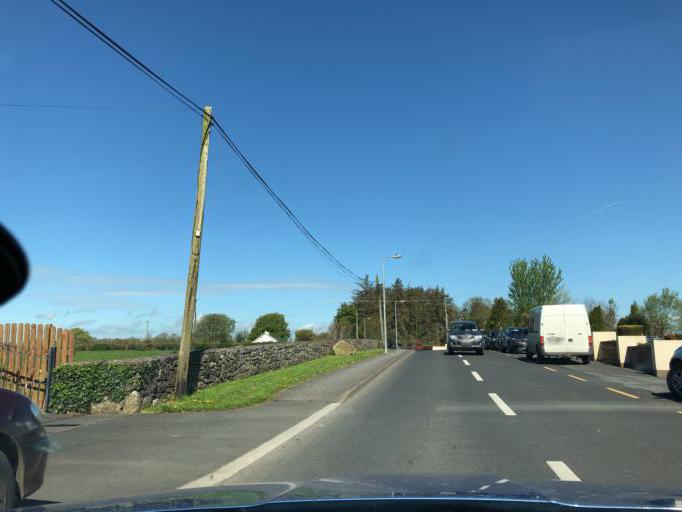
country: IE
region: Connaught
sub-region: County Galway
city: Portumna
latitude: 53.1446
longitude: -8.3689
